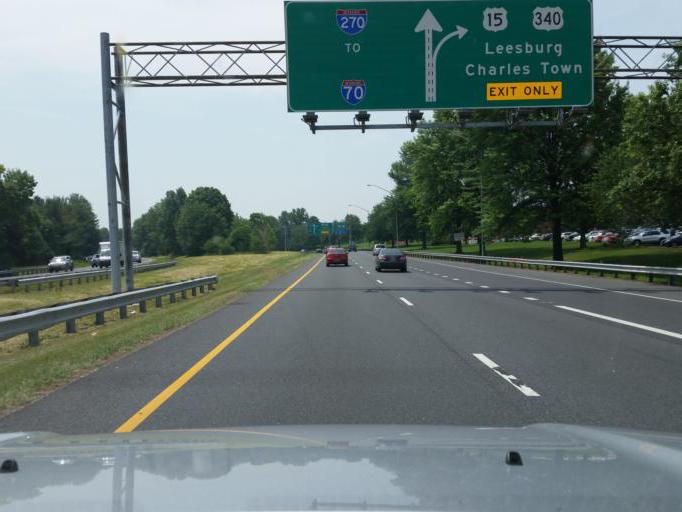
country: US
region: Maryland
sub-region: Frederick County
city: Frederick
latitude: 39.4127
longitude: -77.4360
